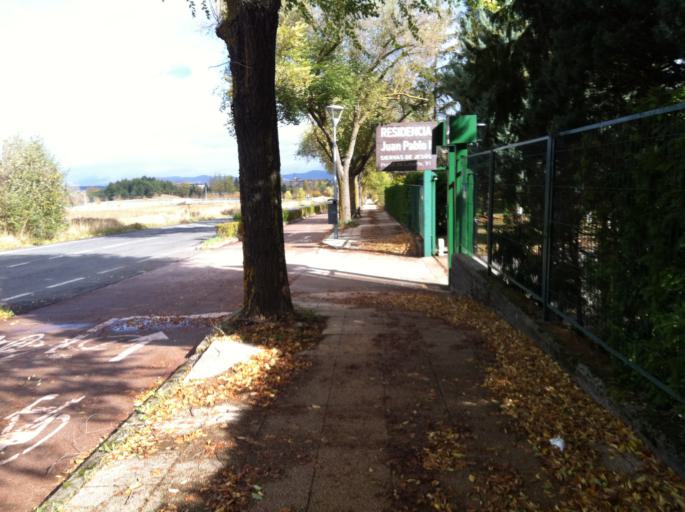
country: ES
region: Basque Country
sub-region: Provincia de Alava
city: Gasteiz / Vitoria
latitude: 42.8295
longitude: -2.6913
